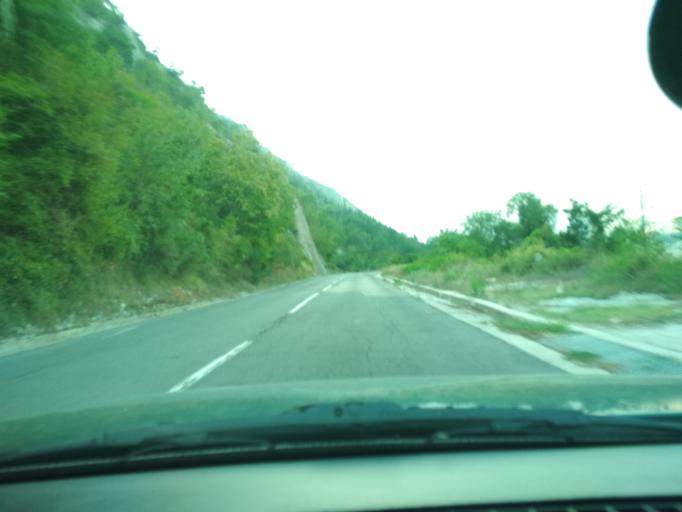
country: ME
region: Kotor
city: Kotor
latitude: 42.4178
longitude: 18.7595
